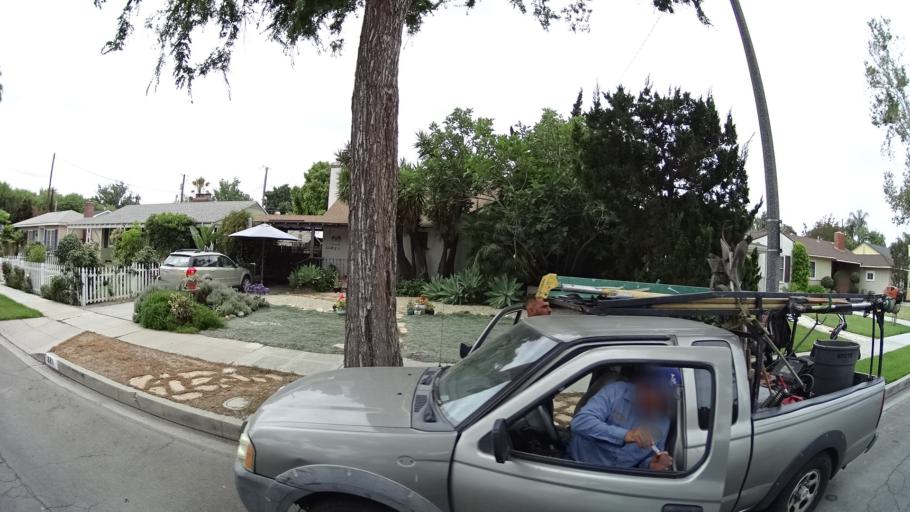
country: US
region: California
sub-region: Los Angeles County
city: Burbank
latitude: 34.1728
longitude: -118.3233
